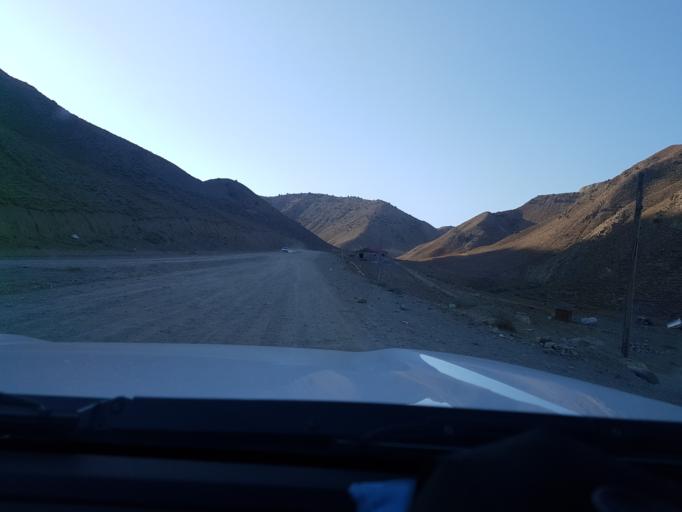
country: TM
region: Ahal
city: Baharly
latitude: 38.4522
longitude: 57.0459
